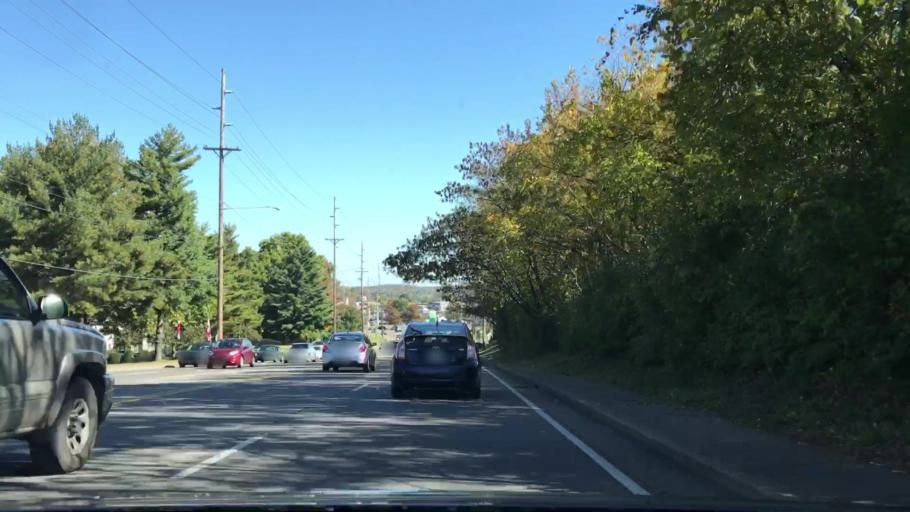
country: US
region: Tennessee
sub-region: Williamson County
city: Brentwood Estates
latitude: 36.0455
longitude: -86.7194
